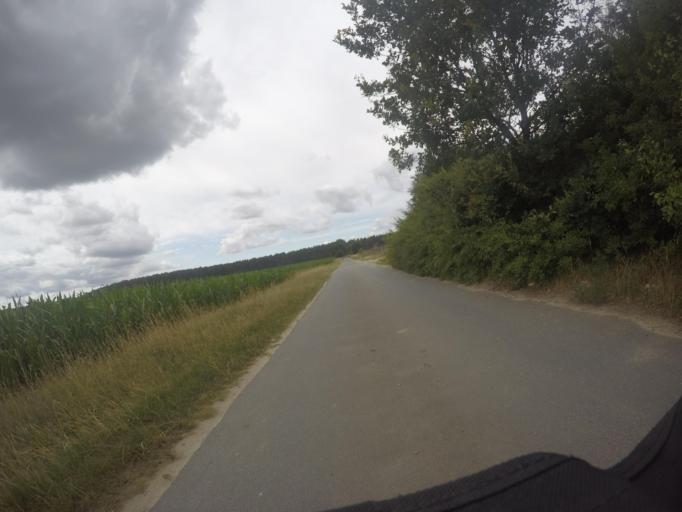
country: DE
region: Lower Saxony
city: Thomasburg
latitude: 53.2289
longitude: 10.6985
